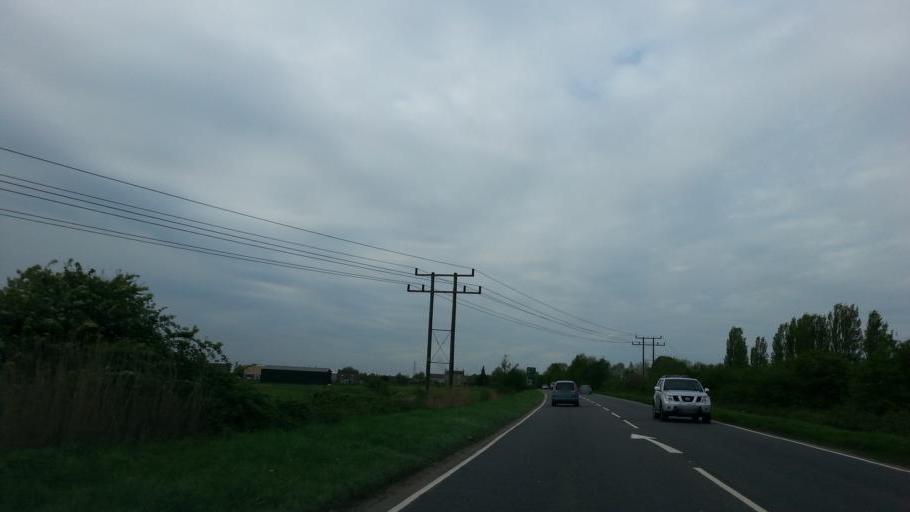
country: GB
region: England
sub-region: Cambridgeshire
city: March
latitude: 52.5419
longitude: 0.0706
